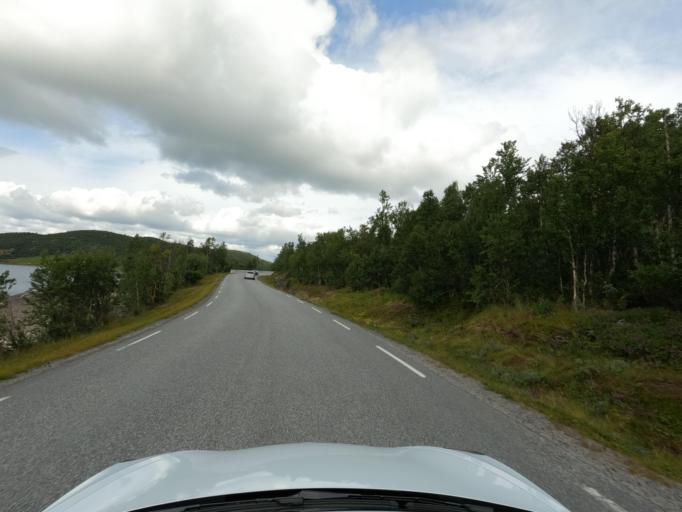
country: NO
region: Telemark
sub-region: Tinn
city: Rjukan
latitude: 59.8149
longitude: 8.3011
